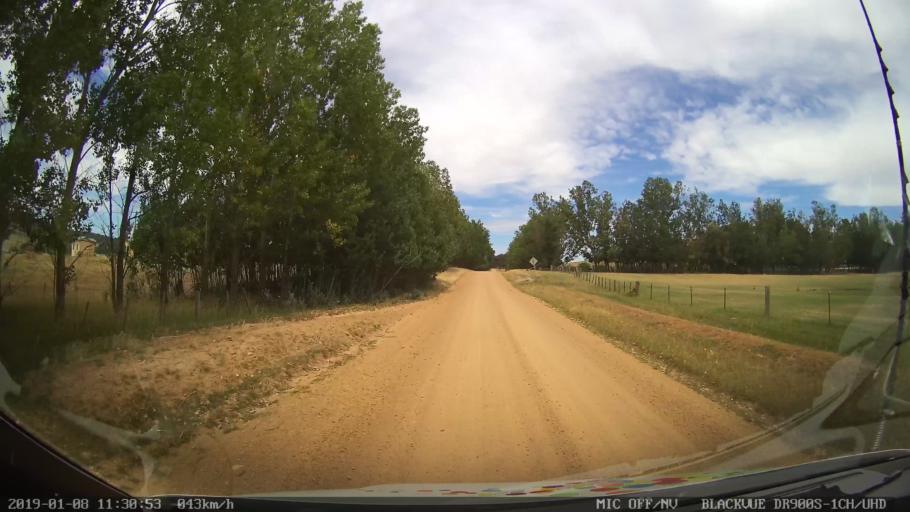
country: AU
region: New South Wales
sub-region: Guyra
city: Guyra
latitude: -30.3099
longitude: 151.5418
